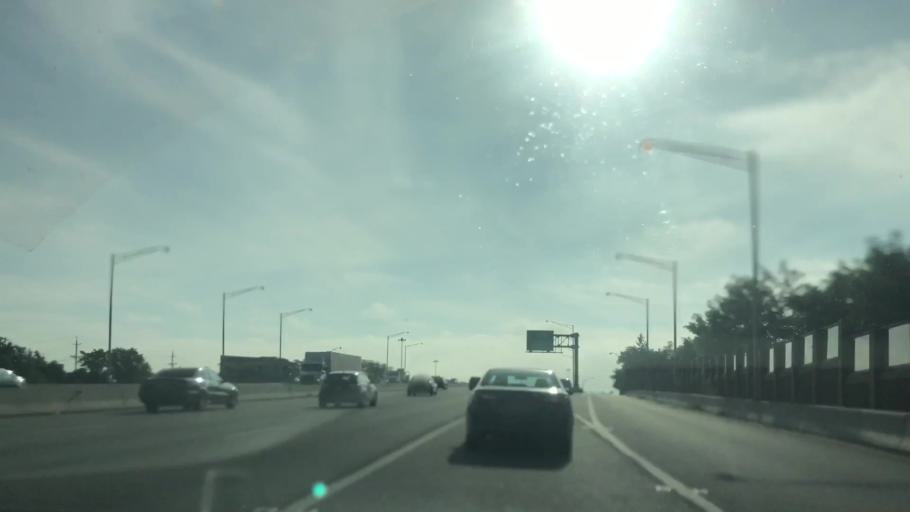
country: US
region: New Jersey
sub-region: Bergen County
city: Lyndhurst
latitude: 40.8267
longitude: -74.1321
